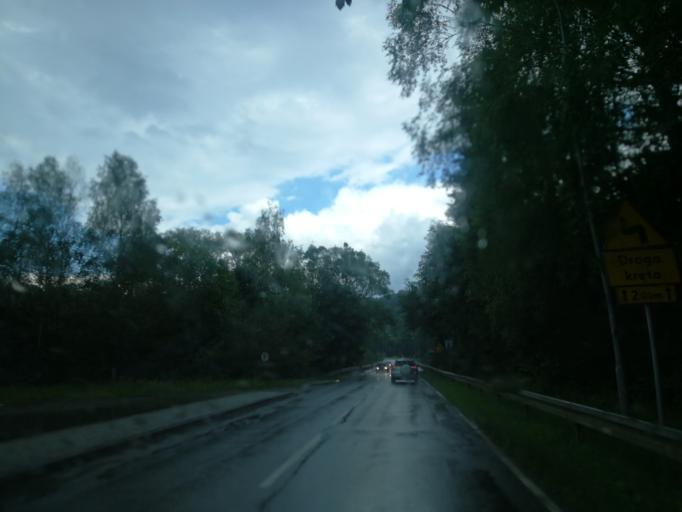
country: PL
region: Subcarpathian Voivodeship
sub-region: Powiat leski
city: Polanczyk
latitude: 49.4005
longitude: 22.4572
